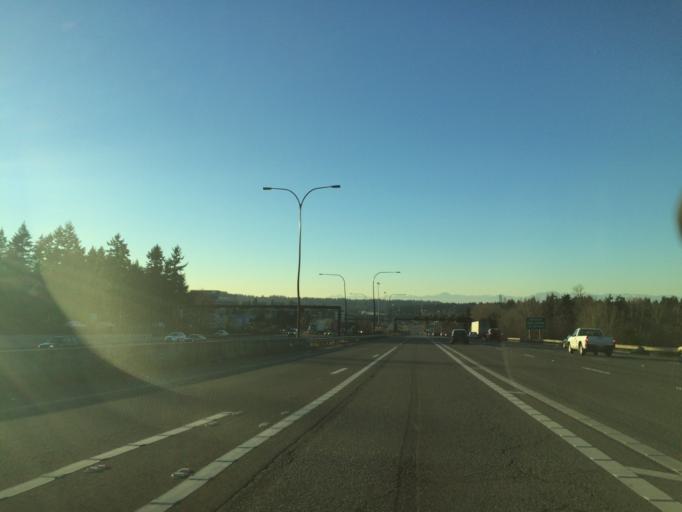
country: US
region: Washington
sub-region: King County
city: Eastgate
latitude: 47.5799
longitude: -122.1582
